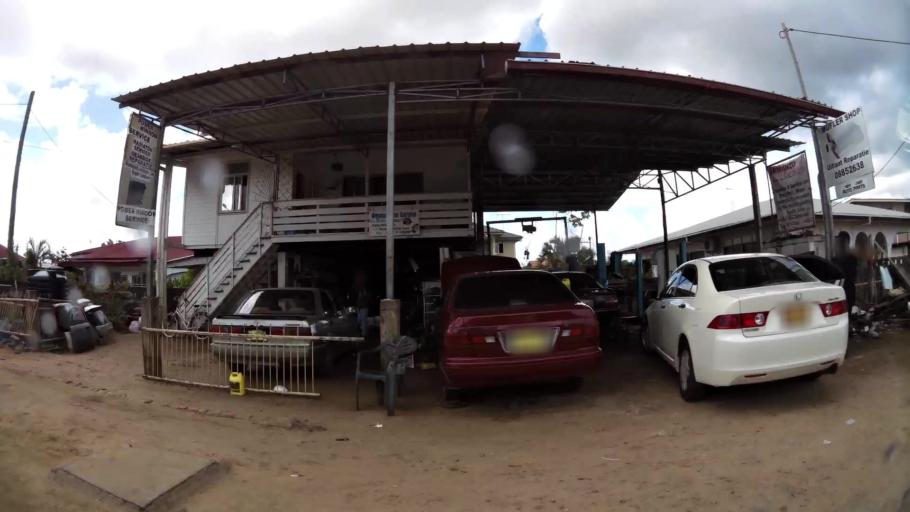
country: SR
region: Paramaribo
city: Paramaribo
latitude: 5.8326
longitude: -55.2040
